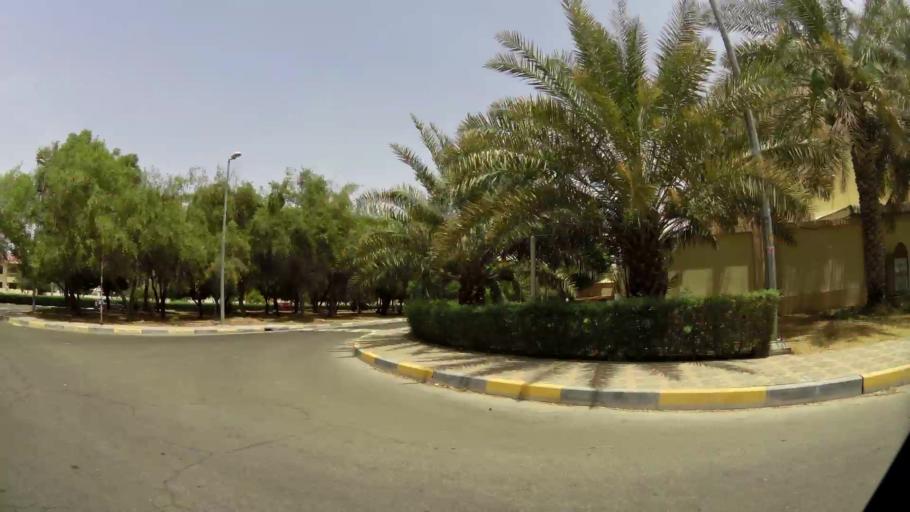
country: AE
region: Abu Dhabi
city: Al Ain
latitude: 24.2054
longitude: 55.7122
